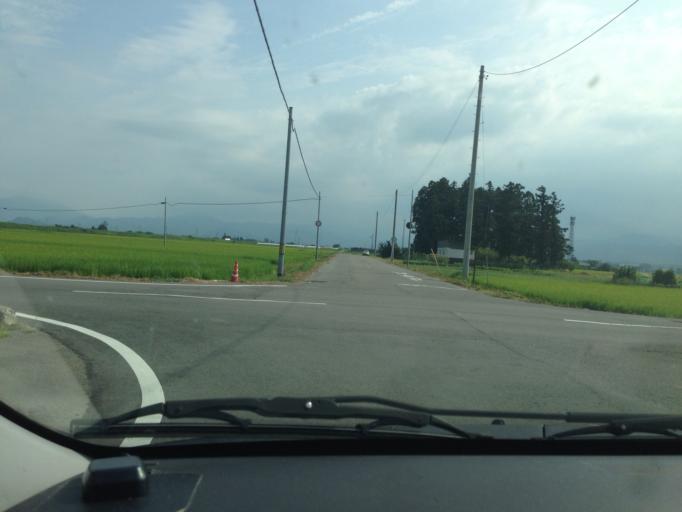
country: JP
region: Fukushima
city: Kitakata
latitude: 37.5515
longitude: 139.8509
